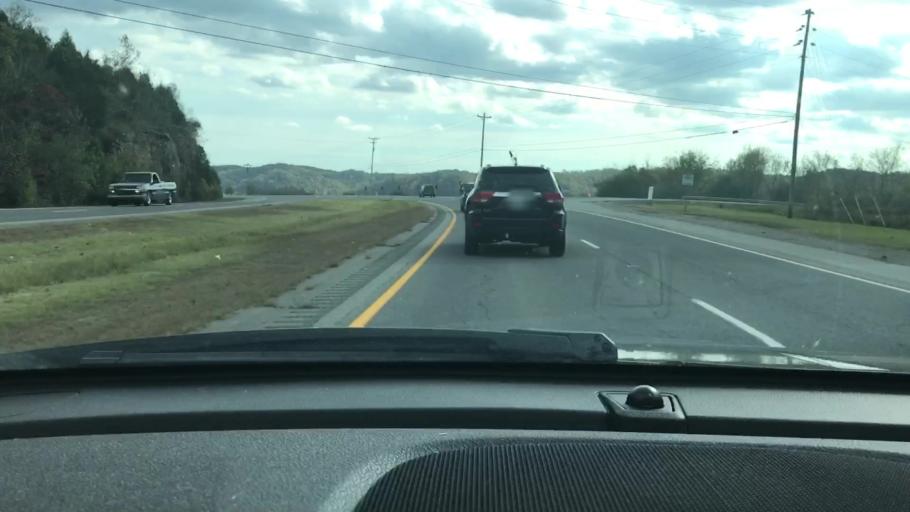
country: US
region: Tennessee
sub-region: Cheatham County
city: Ashland City
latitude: 36.2336
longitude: -87.0191
